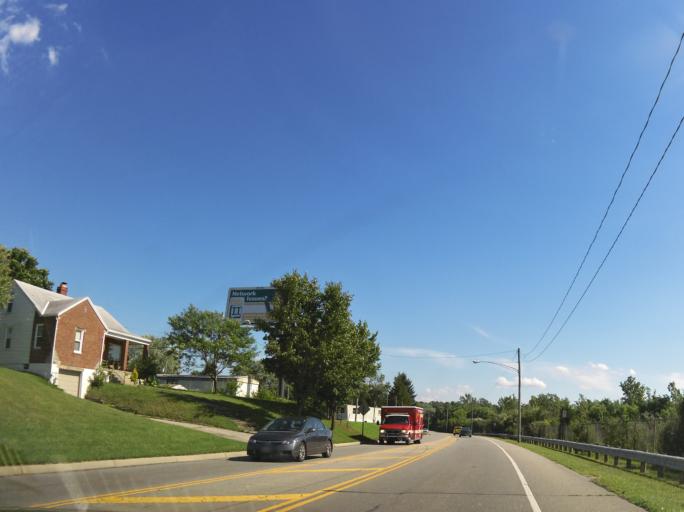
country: US
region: Ohio
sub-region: Greene County
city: Wright-Patterson AFB
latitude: 39.7918
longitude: -84.0450
